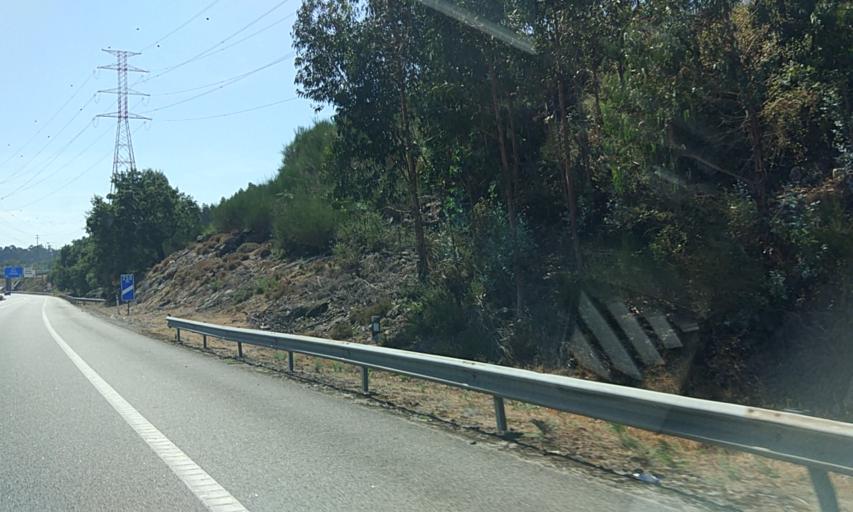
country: PT
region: Porto
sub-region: Paredes
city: Baltar
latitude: 41.1722
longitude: -8.3835
